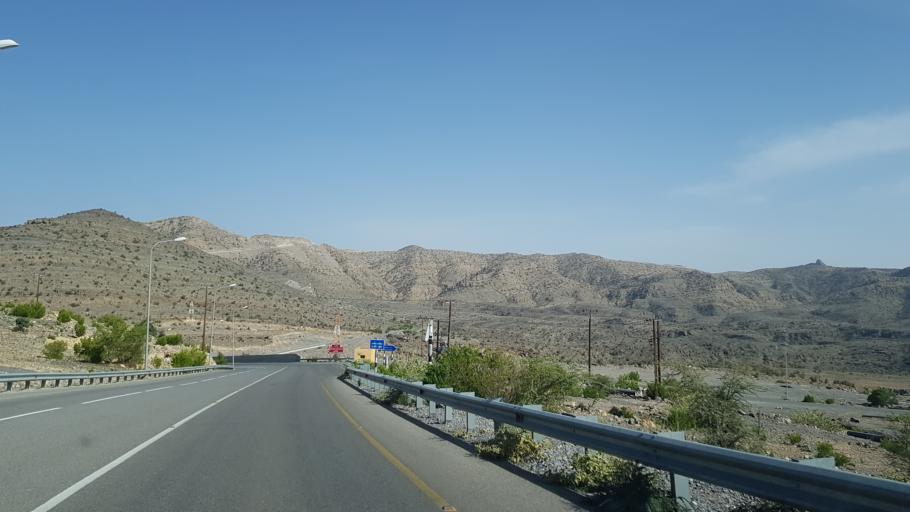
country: OM
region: Muhafazat ad Dakhiliyah
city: Izki
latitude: 23.0737
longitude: 57.7072
